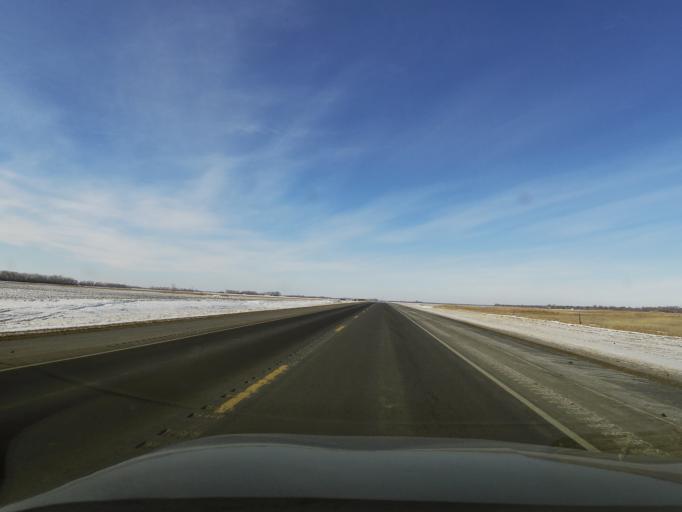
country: US
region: North Dakota
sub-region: Walsh County
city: Grafton
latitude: 48.4126
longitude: -97.4648
